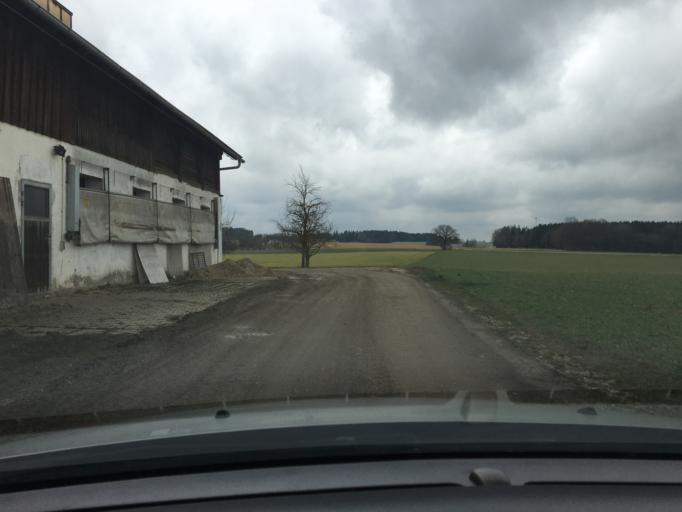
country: DE
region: Bavaria
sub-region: Lower Bavaria
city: Gangkofen
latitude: 48.4488
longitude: 12.5869
